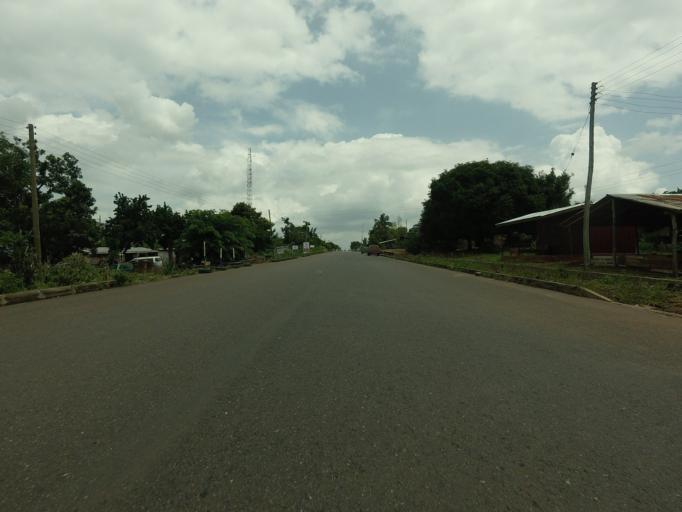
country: GH
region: Volta
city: Ho
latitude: 6.5341
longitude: 0.2301
